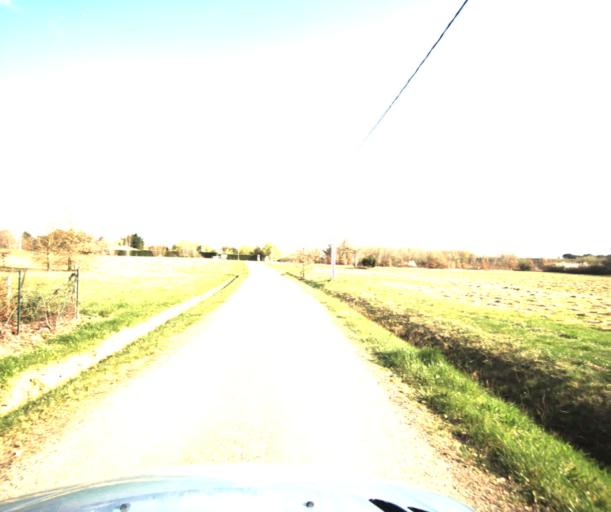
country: FR
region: Midi-Pyrenees
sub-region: Departement du Tarn-et-Garonne
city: Campsas
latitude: 43.9319
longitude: 1.3098
